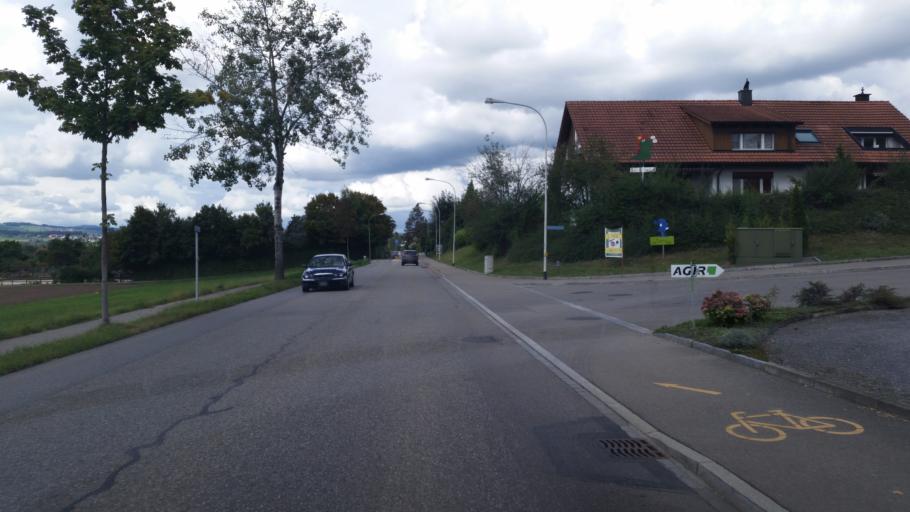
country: CH
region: Zurich
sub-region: Bezirk Affoltern
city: Ottenbach
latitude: 47.2751
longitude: 8.4109
